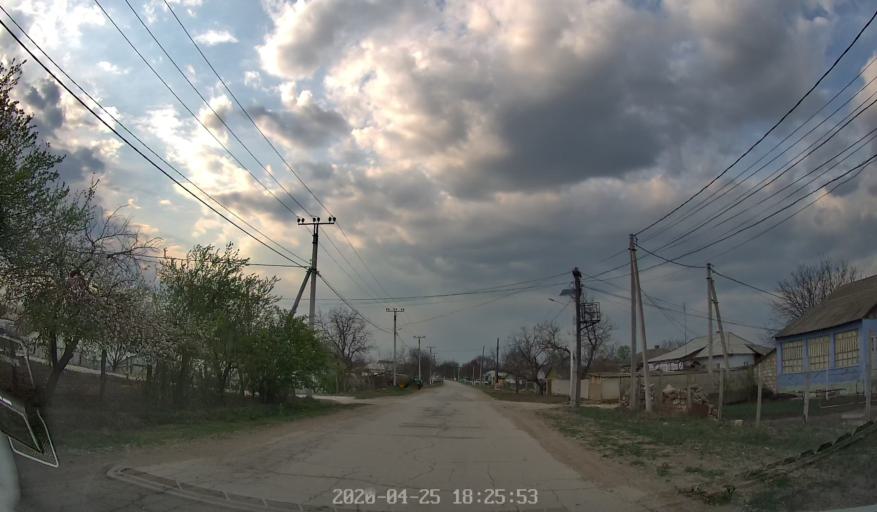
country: MD
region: Criuleni
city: Criuleni
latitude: 47.1638
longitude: 29.1280
